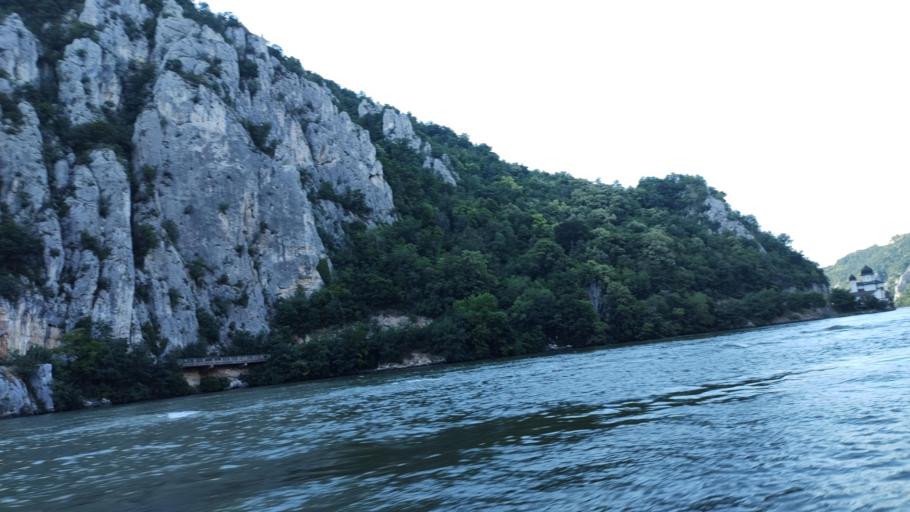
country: RO
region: Mehedinti
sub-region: Comuna Dubova
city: Dubova
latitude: 44.6346
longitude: 22.2910
